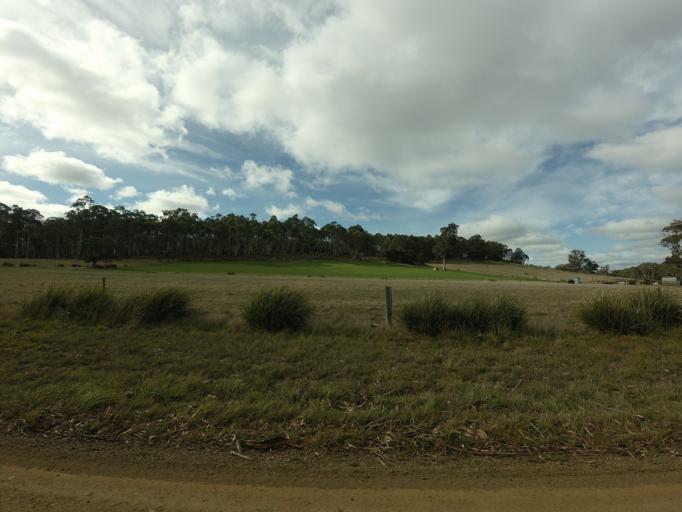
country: AU
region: Tasmania
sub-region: Brighton
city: Bridgewater
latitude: -42.4261
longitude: 147.4292
